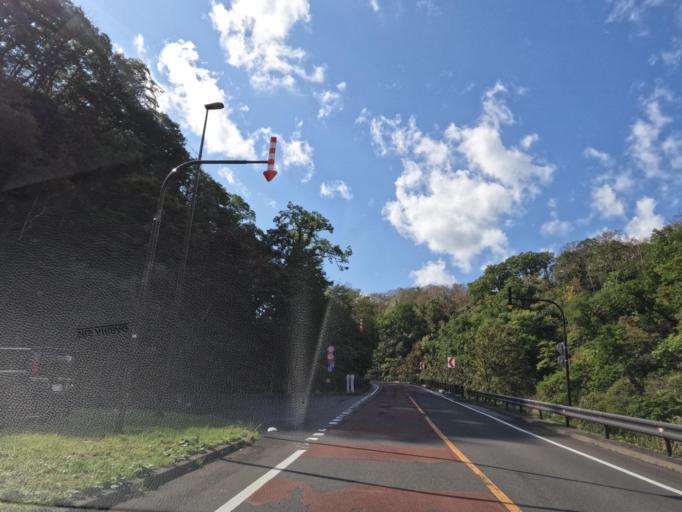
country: JP
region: Hokkaido
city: Shiraoi
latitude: 42.4821
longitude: 141.1457
